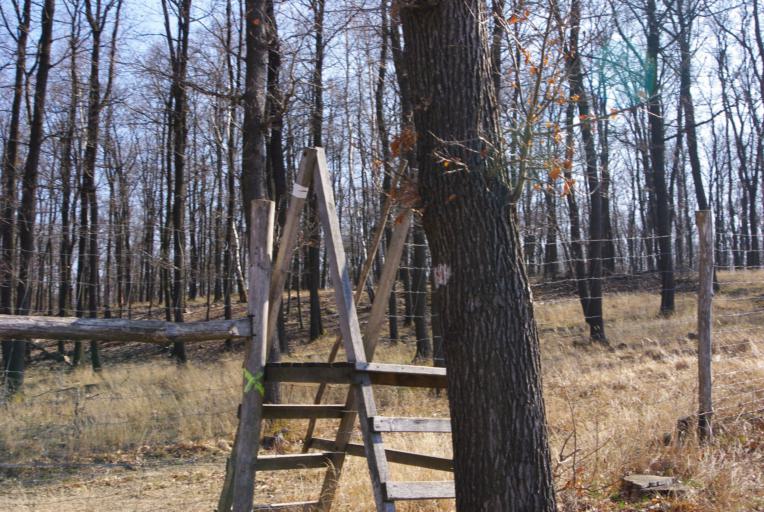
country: HU
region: Pest
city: Paty
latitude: 47.5178
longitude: 18.8770
